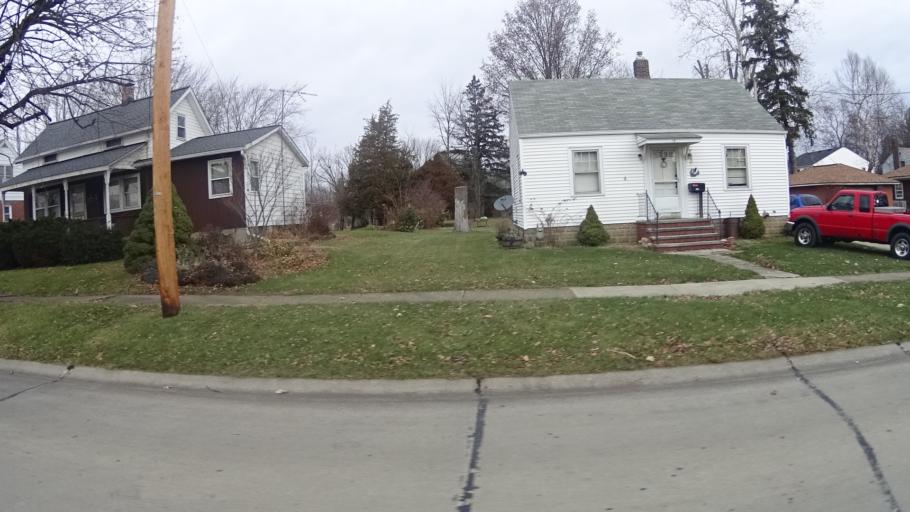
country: US
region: Ohio
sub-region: Lorain County
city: Wellington
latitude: 41.1656
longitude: -82.2112
